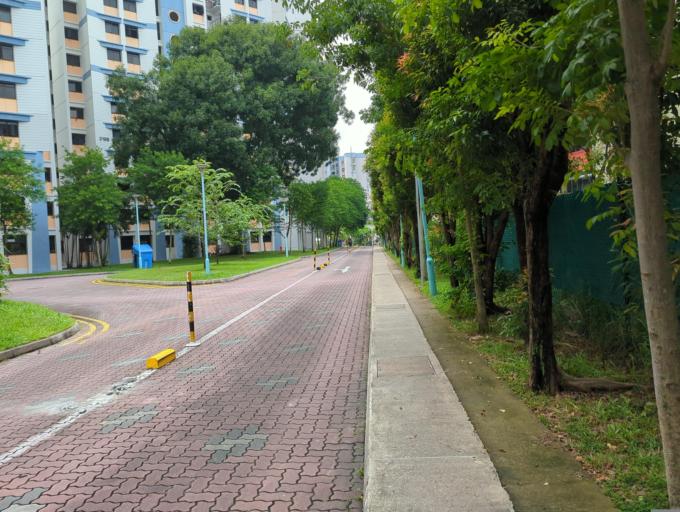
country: MY
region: Johor
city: Kampung Pasir Gudang Baru
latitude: 1.3915
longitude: 103.8912
